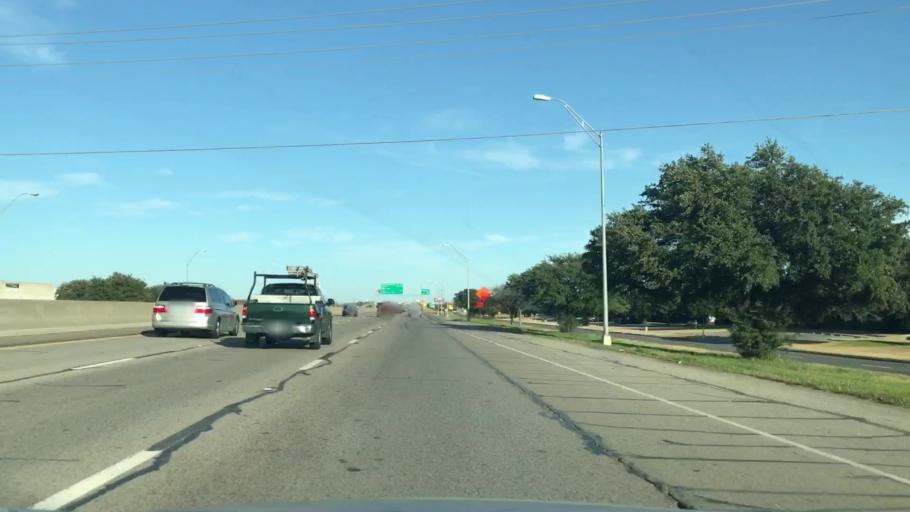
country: US
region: Texas
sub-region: Tarrant County
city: Haltom City
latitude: 32.7901
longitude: -97.2513
